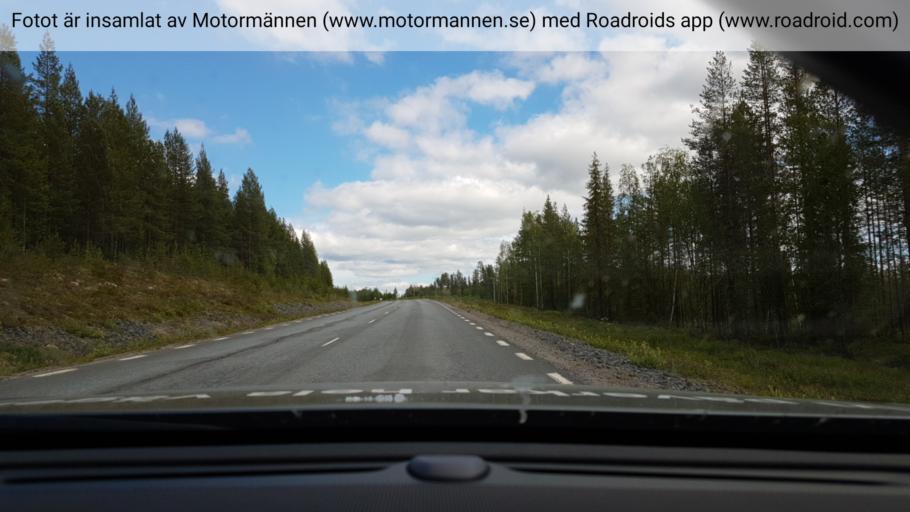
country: SE
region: Vaesterbotten
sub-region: Sorsele Kommun
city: Sorsele
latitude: 65.5378
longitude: 17.5779
